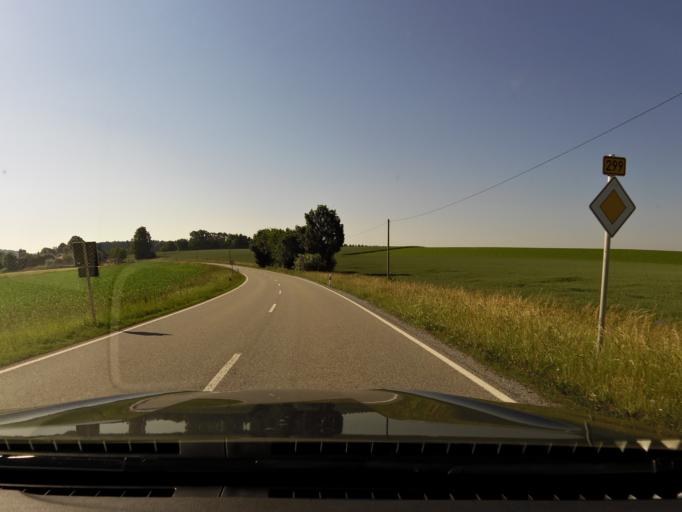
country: DE
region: Bavaria
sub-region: Upper Bavaria
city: Niedertaufkirchen
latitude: 48.3233
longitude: 12.5364
